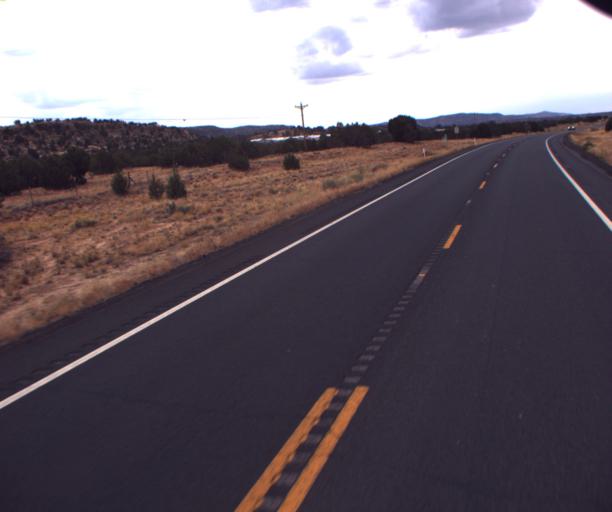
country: US
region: Arizona
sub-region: Coconino County
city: Kaibito
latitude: 36.4777
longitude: -110.6534
